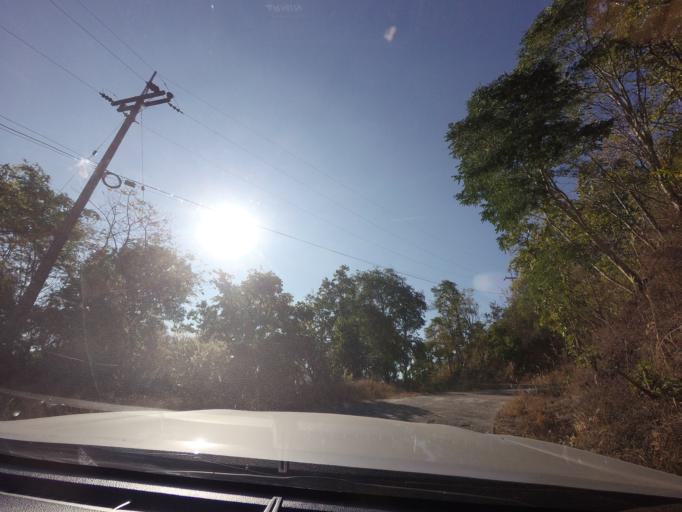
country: TH
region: Lampang
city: Chae Hom
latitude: 18.6157
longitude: 99.6458
